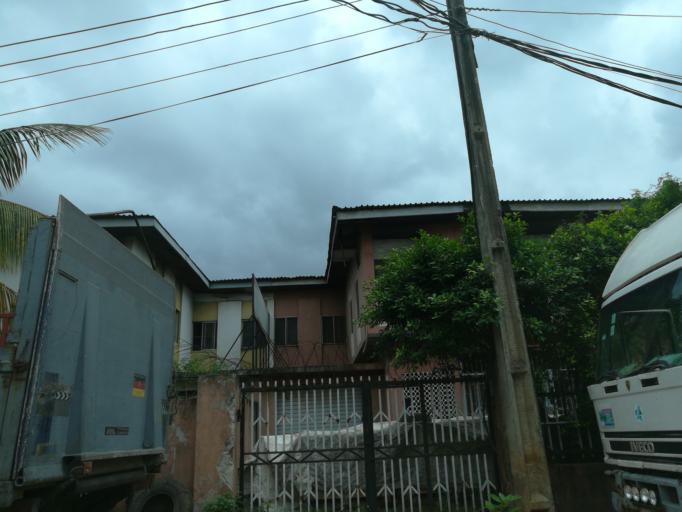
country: NG
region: Lagos
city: Oshodi
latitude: 6.5546
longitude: 3.3281
